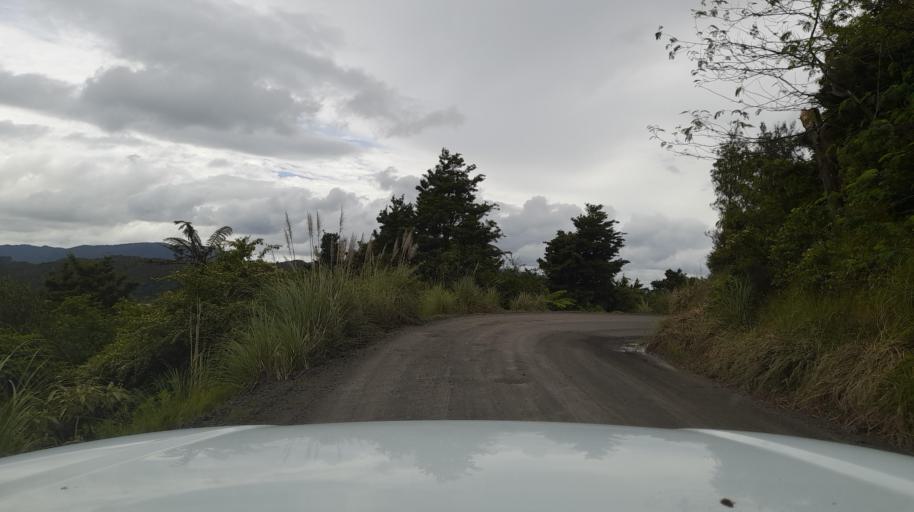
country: NZ
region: Northland
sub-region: Far North District
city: Kaitaia
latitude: -35.3156
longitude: 173.3437
